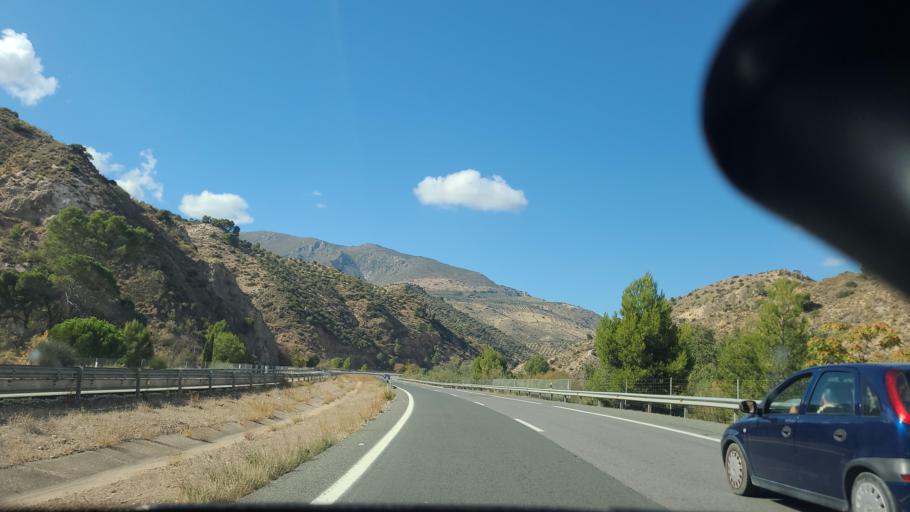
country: ES
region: Andalusia
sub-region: Provincia de Jaen
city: Cambil
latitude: 37.6579
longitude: -3.6074
